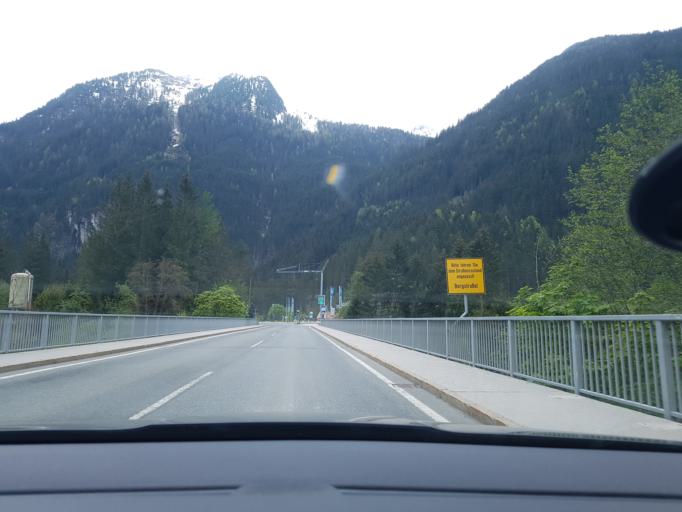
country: AT
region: Salzburg
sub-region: Politischer Bezirk Zell am See
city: Krimml
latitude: 47.2150
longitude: 12.1708
